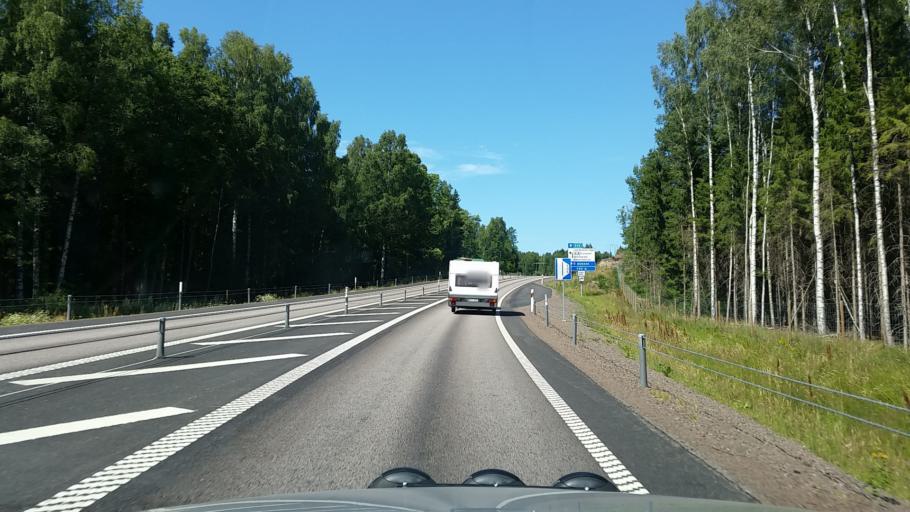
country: SE
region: Vaestra Goetaland
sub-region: Amals Kommun
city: Amal
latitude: 58.8940
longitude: 12.5715
